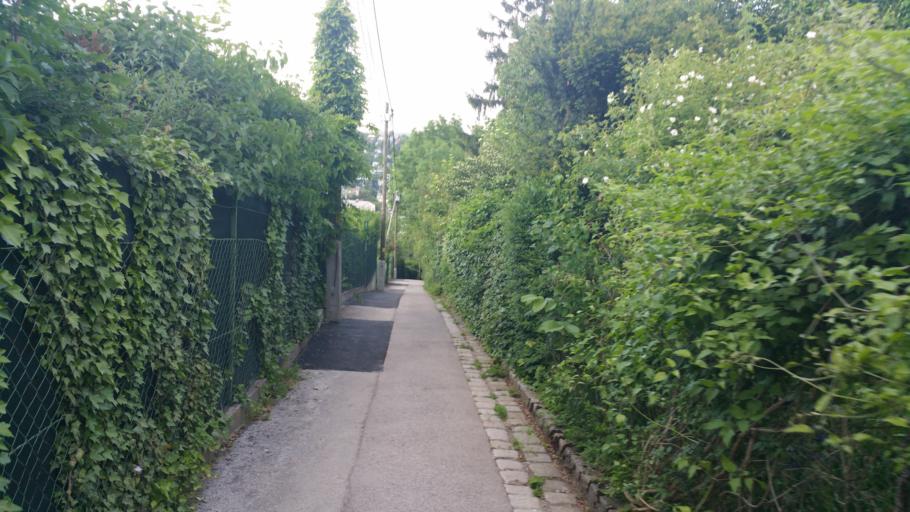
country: AT
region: Vienna
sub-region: Wien Stadt
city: Vienna
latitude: 48.2248
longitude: 16.2940
